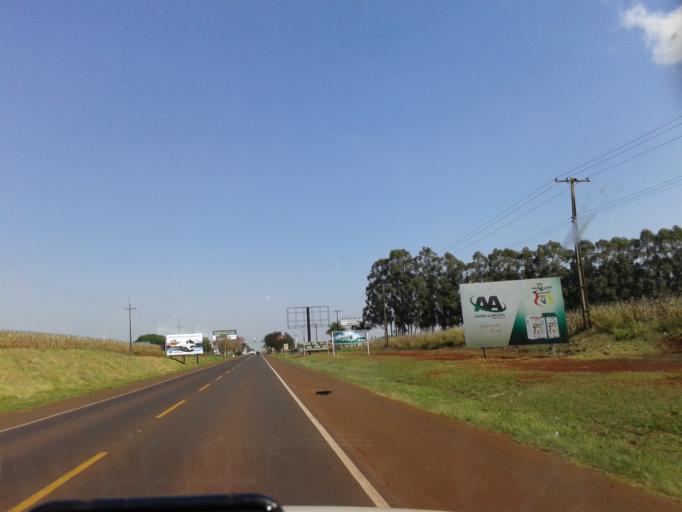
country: PY
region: Alto Parana
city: Santa Rita
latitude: -25.7445
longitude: -55.0519
